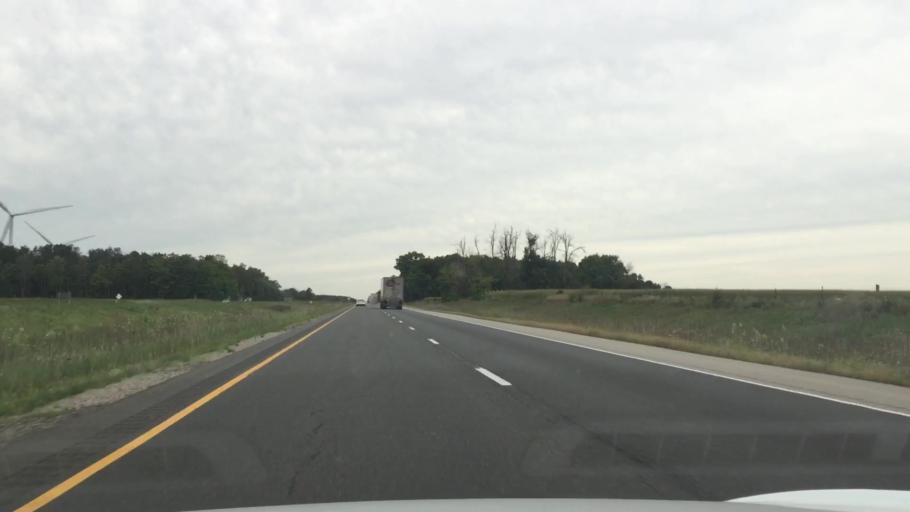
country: CA
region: Ontario
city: Lambton Shores
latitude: 42.9924
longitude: -81.7538
